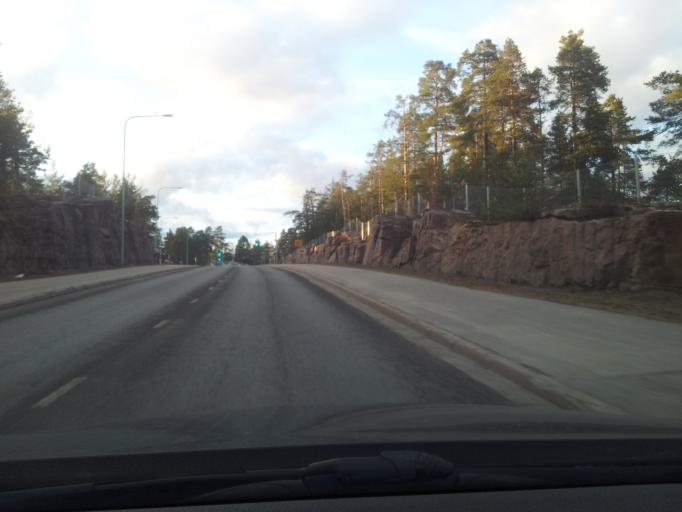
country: FI
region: Uusimaa
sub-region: Helsinki
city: Koukkuniemi
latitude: 60.1742
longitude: 24.7443
